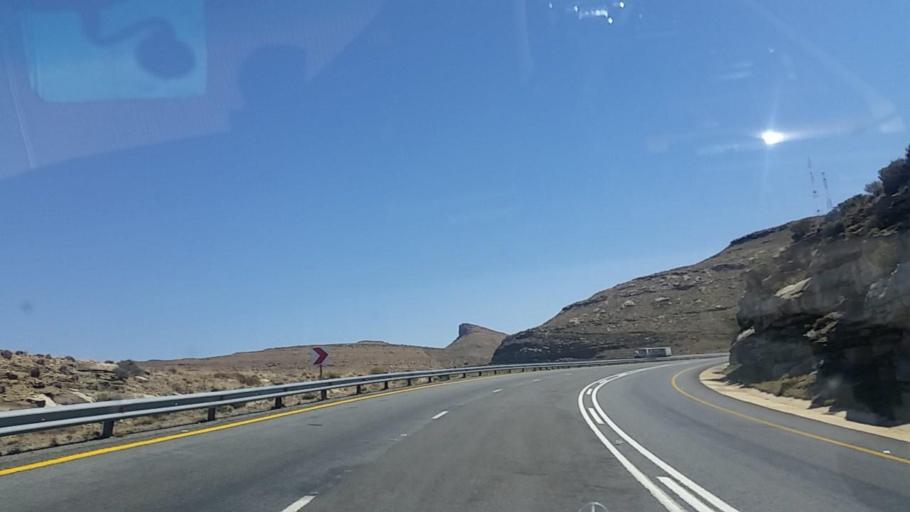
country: ZA
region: Eastern Cape
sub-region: Chris Hani District Municipality
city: Middelburg
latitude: -31.8412
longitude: 24.8668
